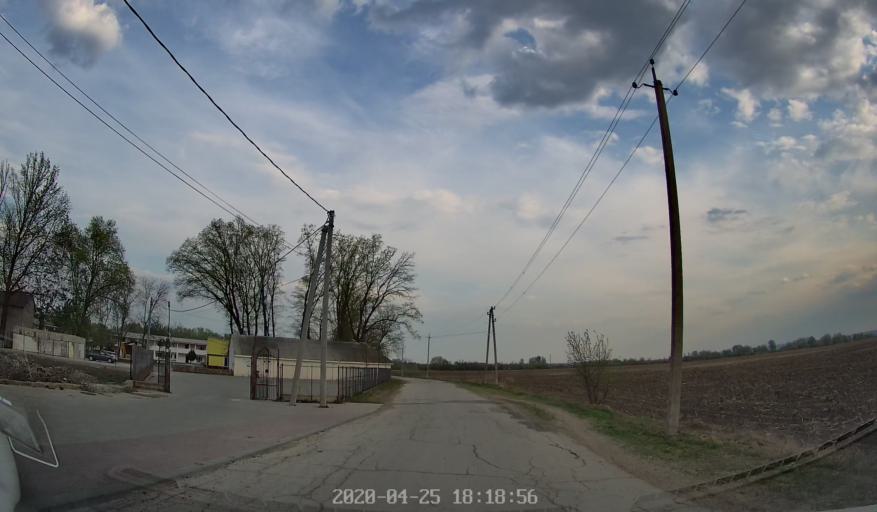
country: MD
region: Criuleni
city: Criuleni
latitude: 47.1616
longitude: 29.1291
